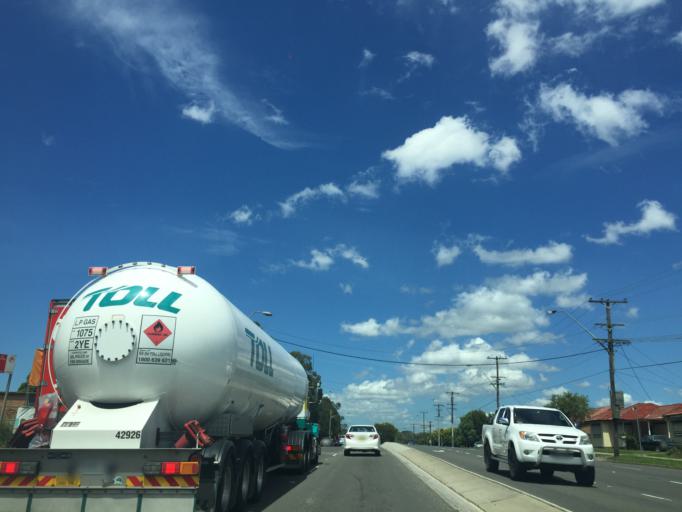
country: AU
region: New South Wales
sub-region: Canterbury
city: Belfield
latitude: -33.9020
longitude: 151.0648
